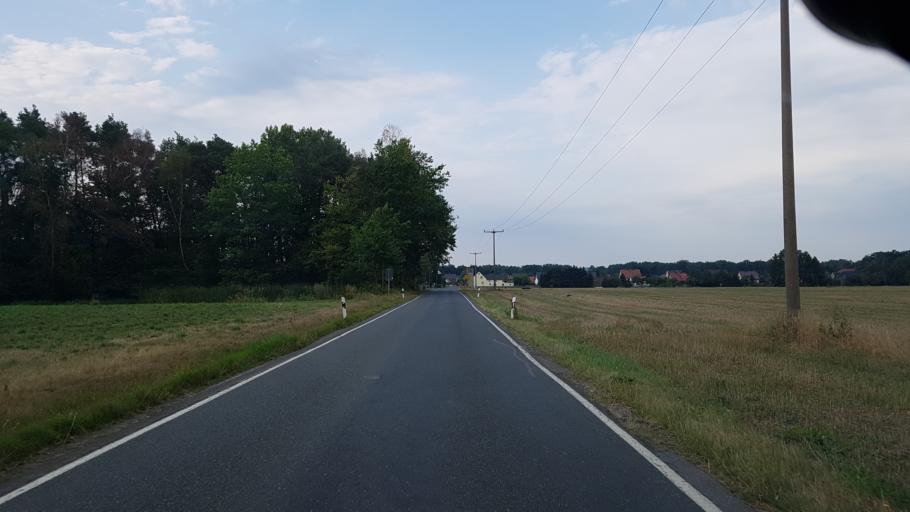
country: DE
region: Brandenburg
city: Lindenau
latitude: 51.4064
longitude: 13.7227
